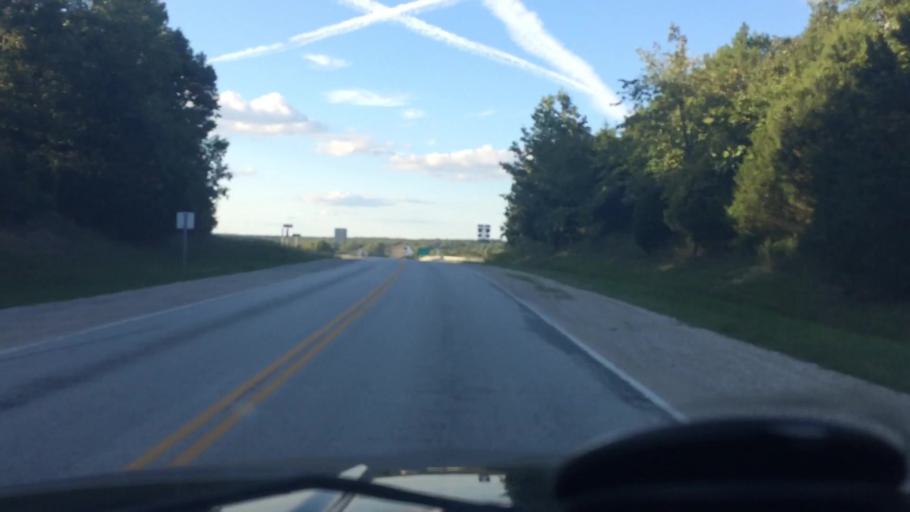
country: US
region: Missouri
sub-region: Webster County
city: Marshfield
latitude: 37.2998
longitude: -92.9997
